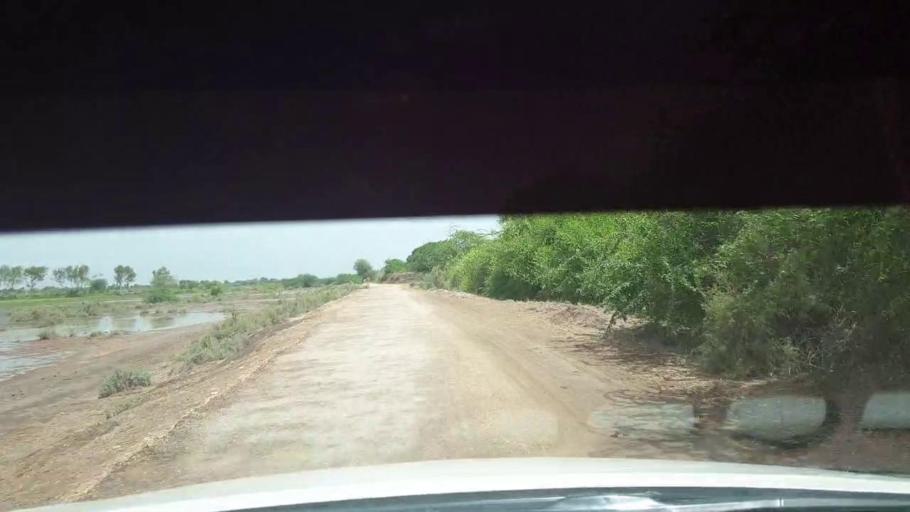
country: PK
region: Sindh
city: Kadhan
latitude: 24.5088
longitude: 68.9776
